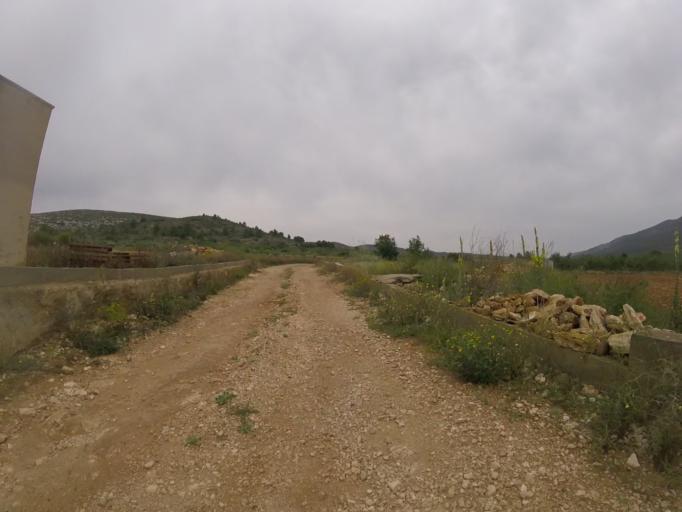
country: ES
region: Valencia
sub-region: Provincia de Castello
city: Alcala de Xivert
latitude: 40.2829
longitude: 0.2562
